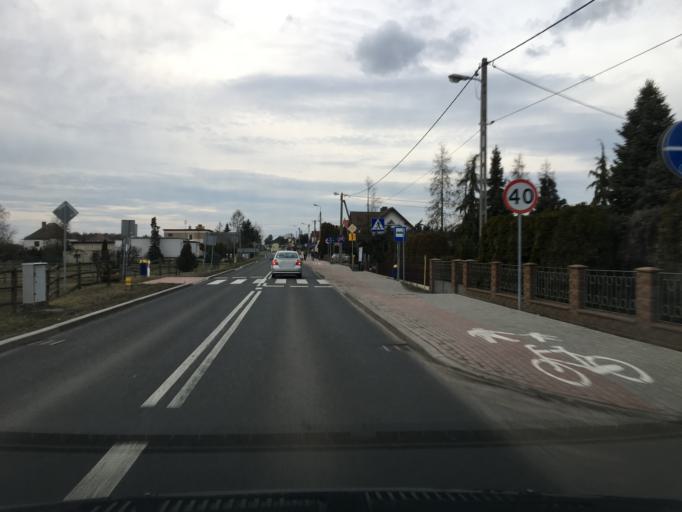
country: PL
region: Opole Voivodeship
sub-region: Powiat krapkowicki
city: Januszkowice
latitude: 50.3920
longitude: 18.1367
